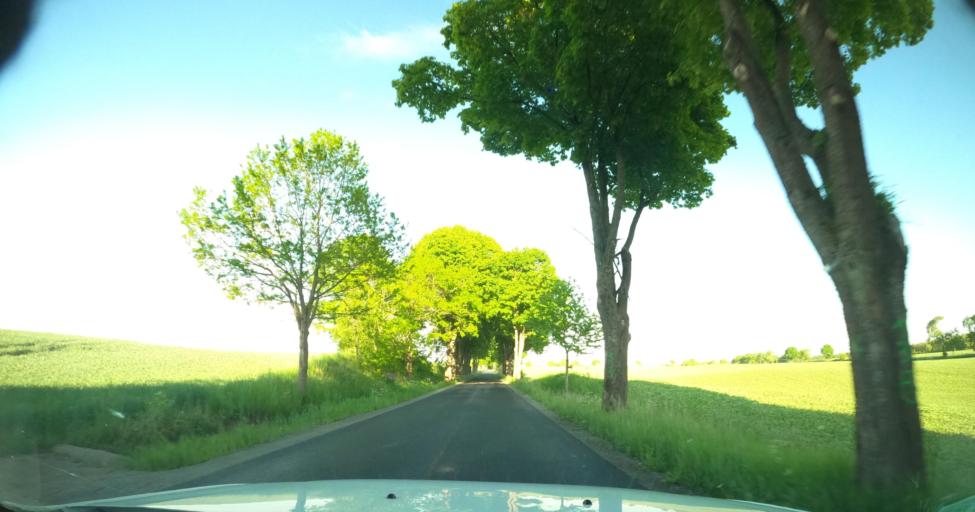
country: PL
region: Warmian-Masurian Voivodeship
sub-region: Powiat braniewski
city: Braniewo
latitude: 54.2823
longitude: 19.8608
